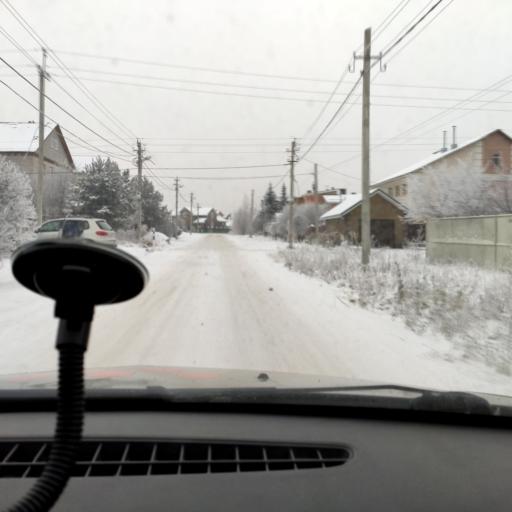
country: RU
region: Bashkortostan
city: Ufa
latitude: 54.6022
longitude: 55.9313
